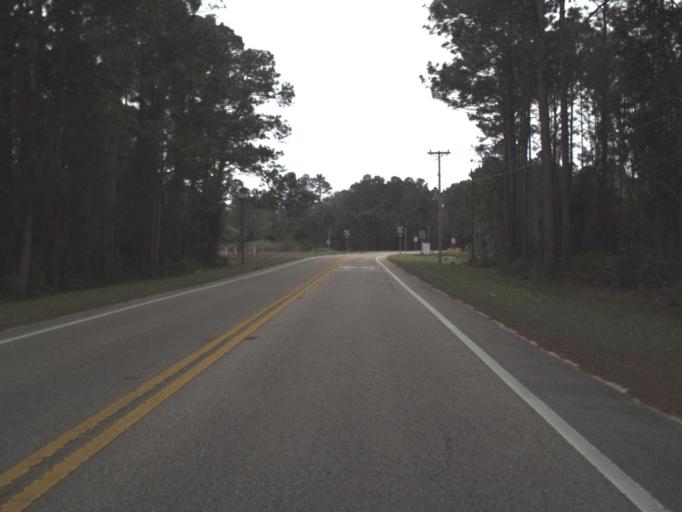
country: US
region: Florida
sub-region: Gulf County
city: Port Saint Joe
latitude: 29.8203
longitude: -85.2832
